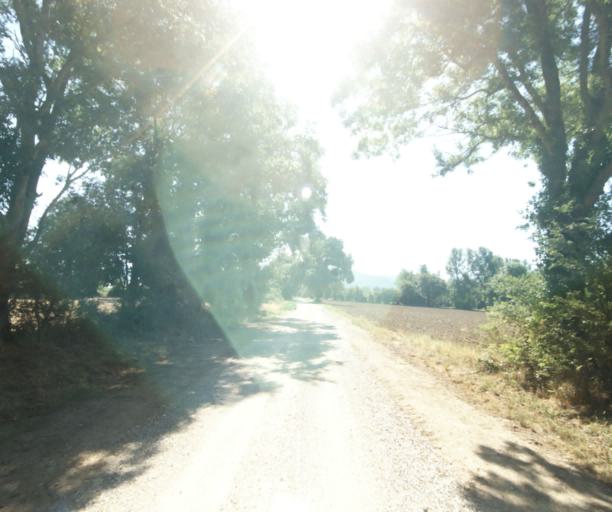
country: FR
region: Midi-Pyrenees
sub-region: Departement de la Haute-Garonne
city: Revel
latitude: 43.4614
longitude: 2.0341
